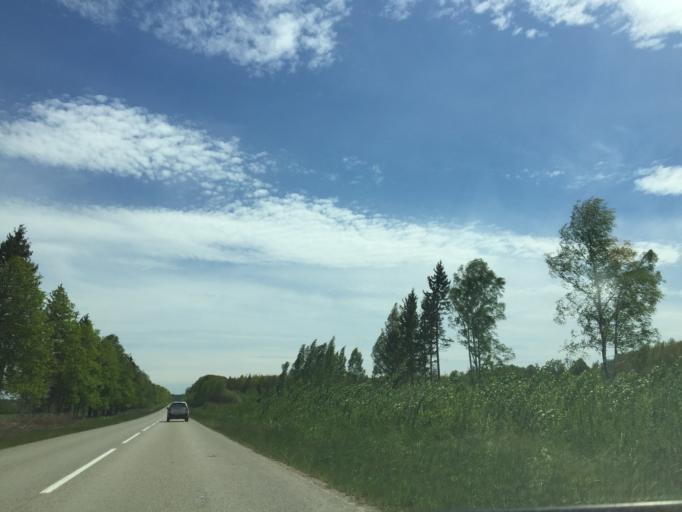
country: LT
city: Linkuva
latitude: 56.0416
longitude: 24.1309
